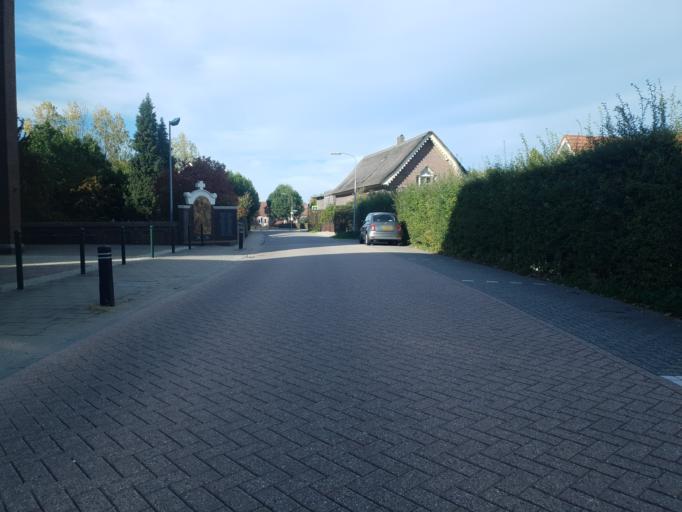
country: NL
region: Gelderland
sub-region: Gemeente Groesbeek
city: Berg en Dal
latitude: 51.8535
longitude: 5.9394
